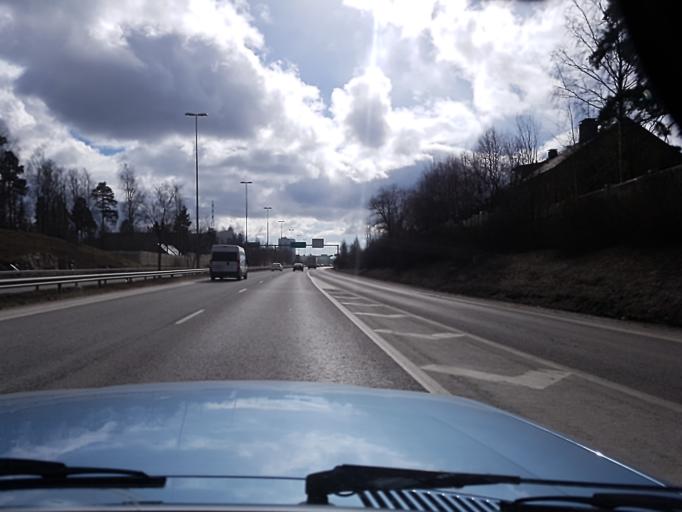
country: FI
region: Uusimaa
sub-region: Helsinki
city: Helsinki
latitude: 60.2260
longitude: 24.9444
